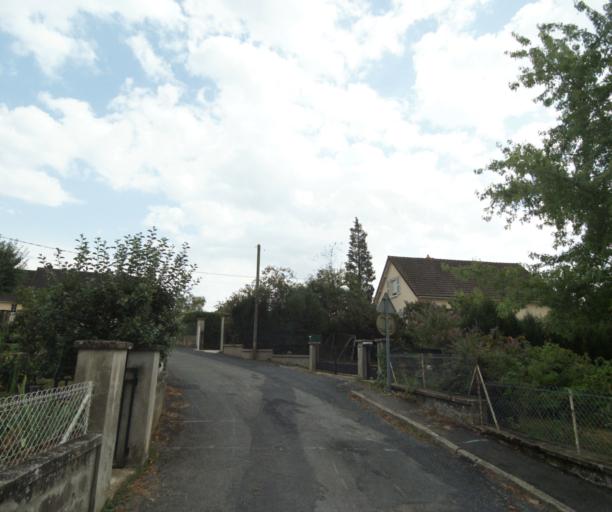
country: FR
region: Bourgogne
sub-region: Departement de Saone-et-Loire
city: Gueugnon
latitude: 46.6042
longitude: 4.0752
